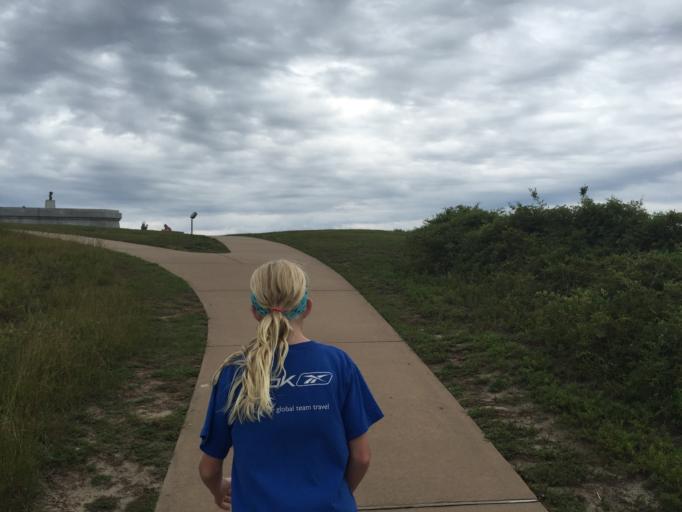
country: US
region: North Carolina
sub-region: Dare County
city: Kill Devil Hills
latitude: 36.0142
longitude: -75.6684
